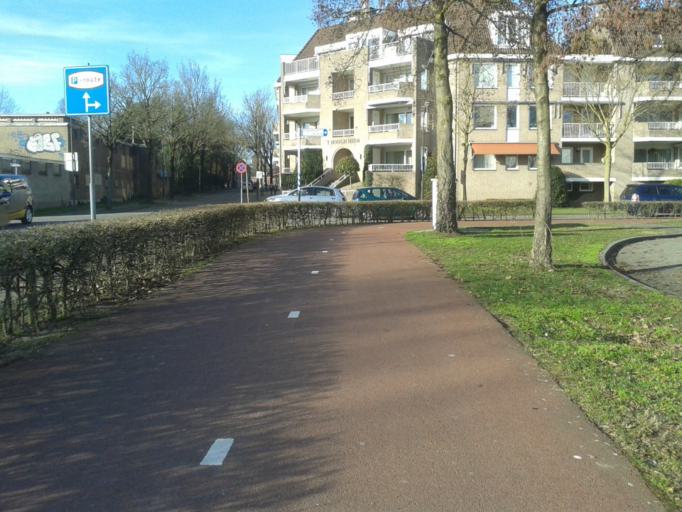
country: NL
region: North Brabant
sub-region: Gemeente Oisterwijk
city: Oisterwijk
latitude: 51.5782
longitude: 5.1894
